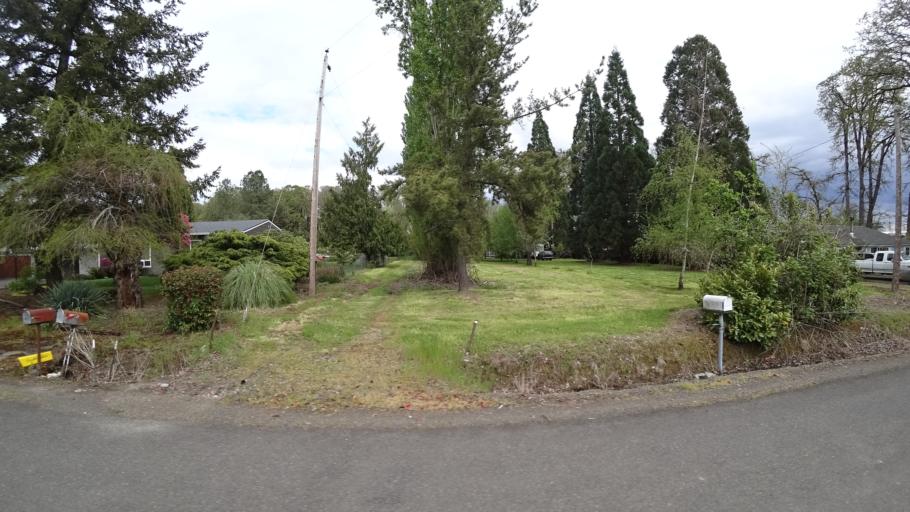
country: US
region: Oregon
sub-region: Washington County
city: Hillsboro
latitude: 45.5534
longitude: -122.9529
